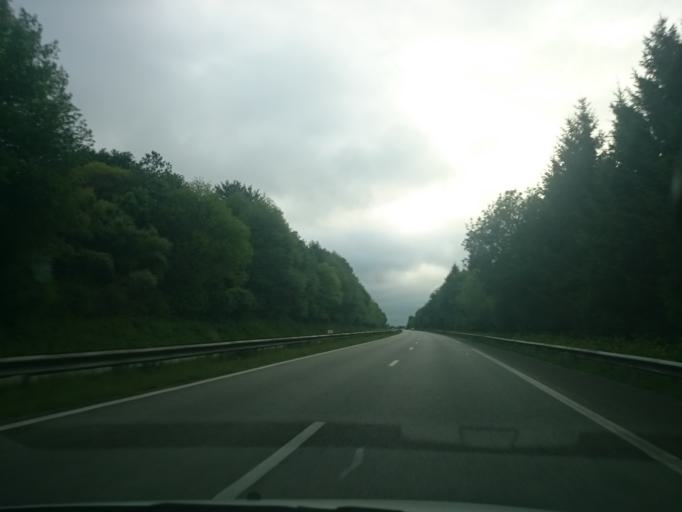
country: FR
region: Brittany
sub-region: Departement du Finistere
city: Saint-Yvi
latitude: 47.9384
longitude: -3.9153
